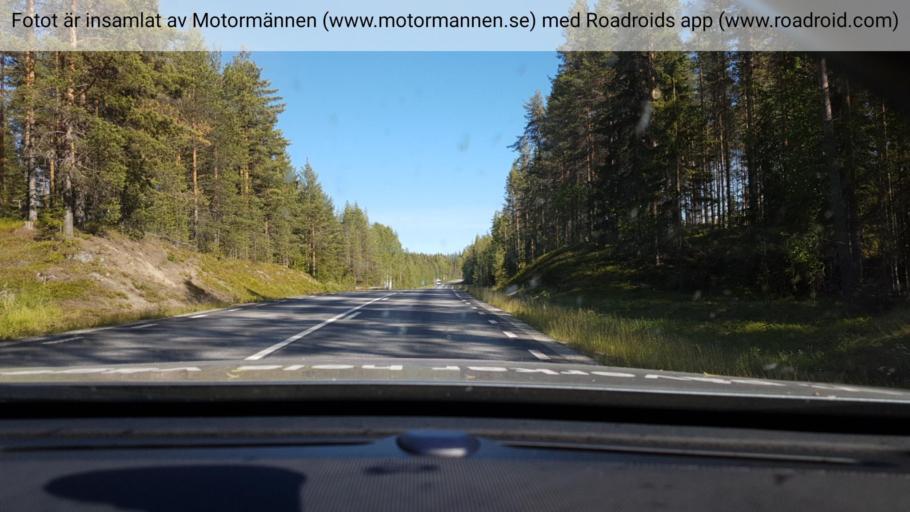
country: SE
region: Vaesterbotten
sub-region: Lycksele Kommun
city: Lycksele
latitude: 64.5134
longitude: 18.8693
